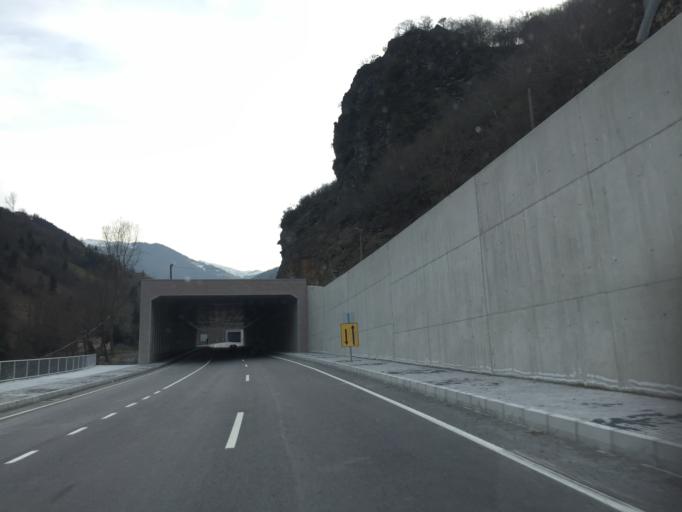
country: TR
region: Trabzon
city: Macka
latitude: 40.7777
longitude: 39.5687
